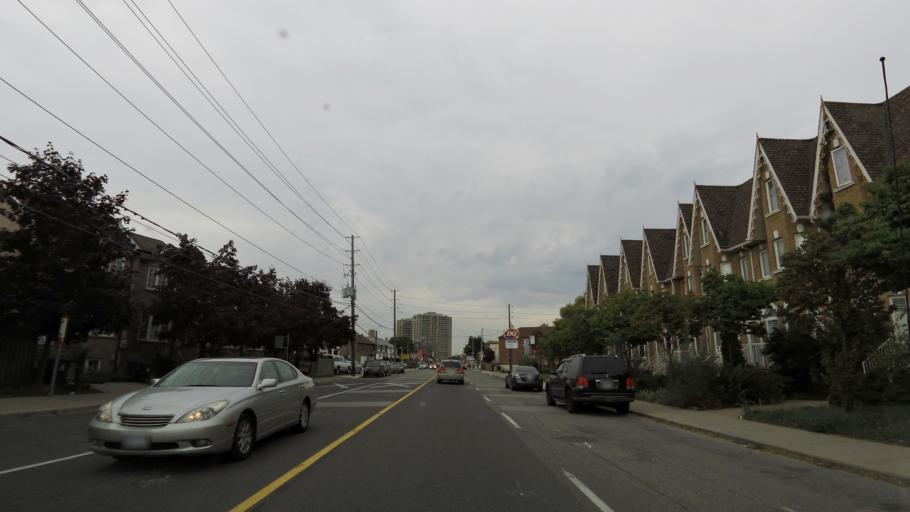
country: CA
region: Ontario
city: Etobicoke
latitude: 43.6949
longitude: -79.5065
